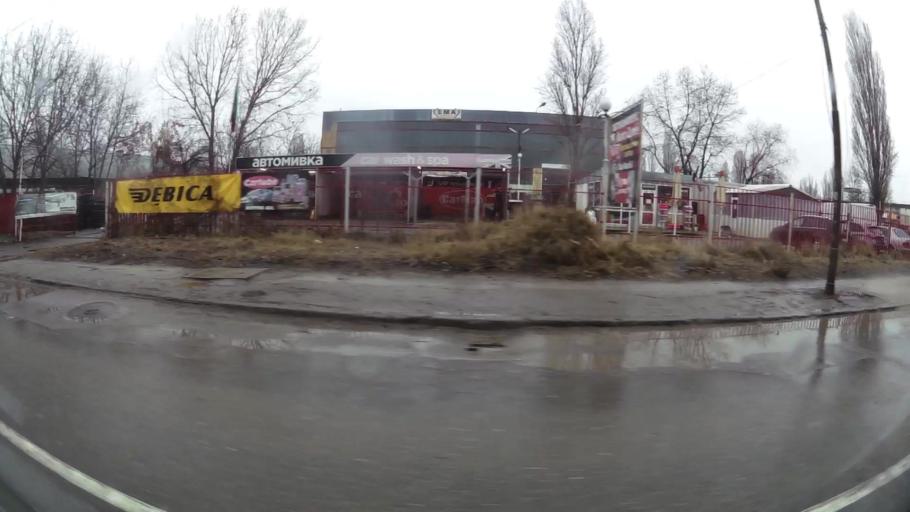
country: BG
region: Sofia-Capital
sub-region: Stolichna Obshtina
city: Sofia
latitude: 42.6634
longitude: 23.4055
